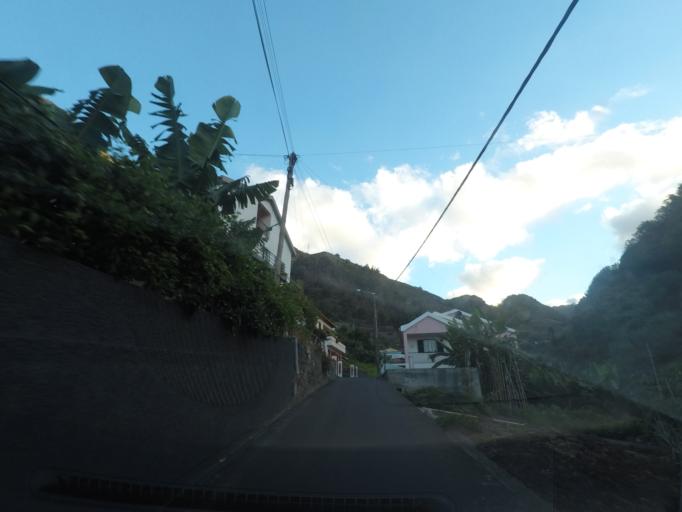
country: PT
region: Madeira
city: Ponta do Sol
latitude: 32.6889
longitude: -17.0749
